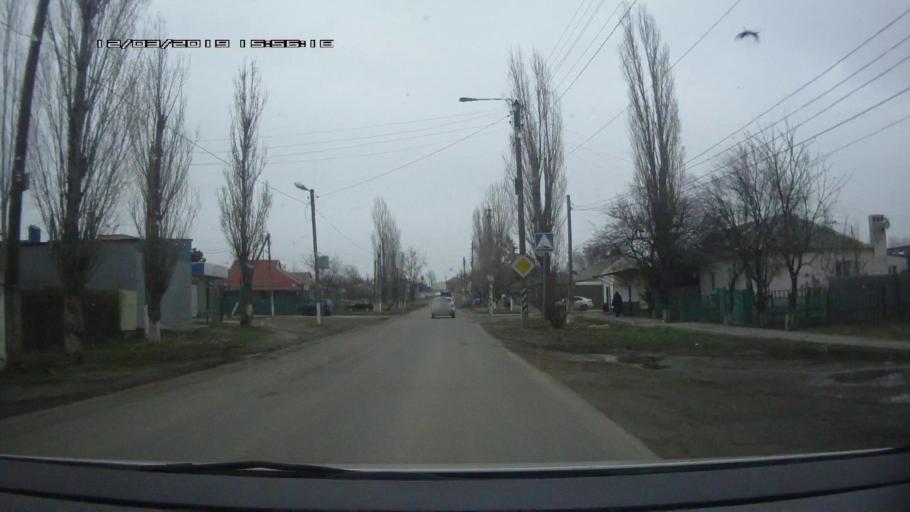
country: RU
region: Rostov
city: Novobataysk
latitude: 46.9000
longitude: 39.7811
